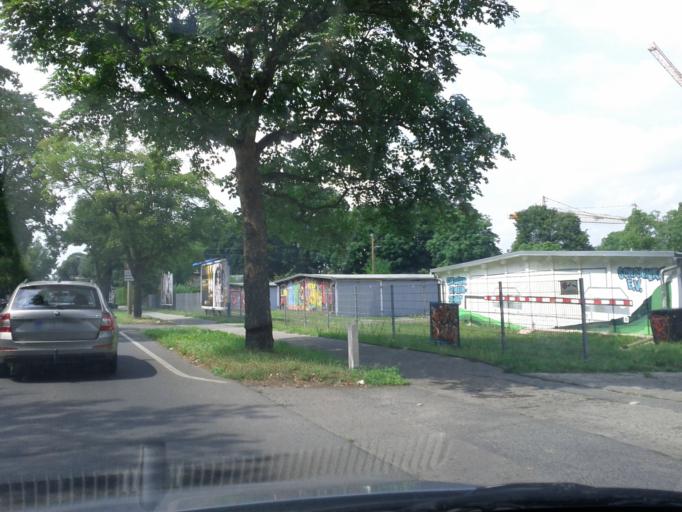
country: DE
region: Berlin
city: Oberschoneweide
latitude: 52.4514
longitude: 13.5369
